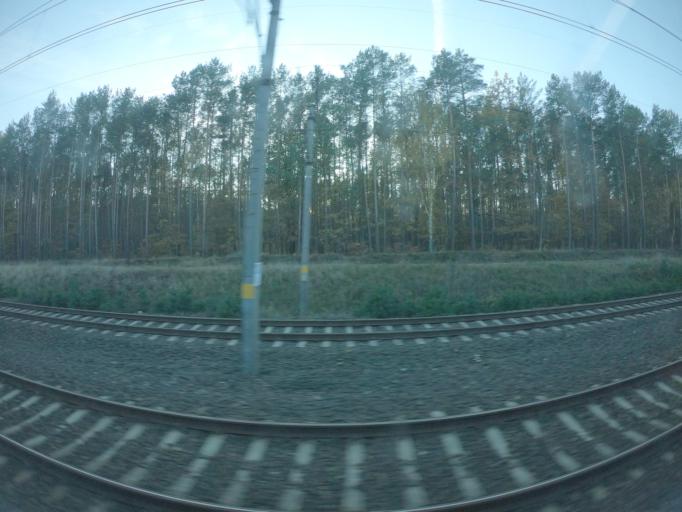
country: PL
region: Lubusz
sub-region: Powiat slubicki
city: Rzepin
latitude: 52.3151
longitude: 14.8572
